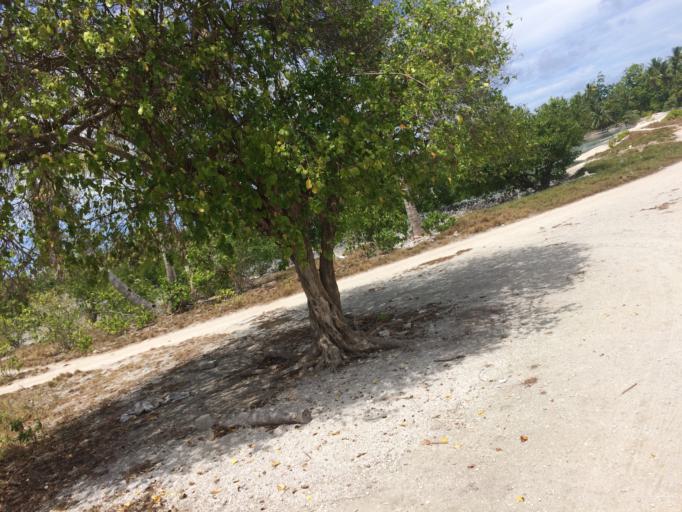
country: KI
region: Gilbert Islands
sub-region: Marakei
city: Rawannawi Village
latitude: 1.9151
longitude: 172.9458
